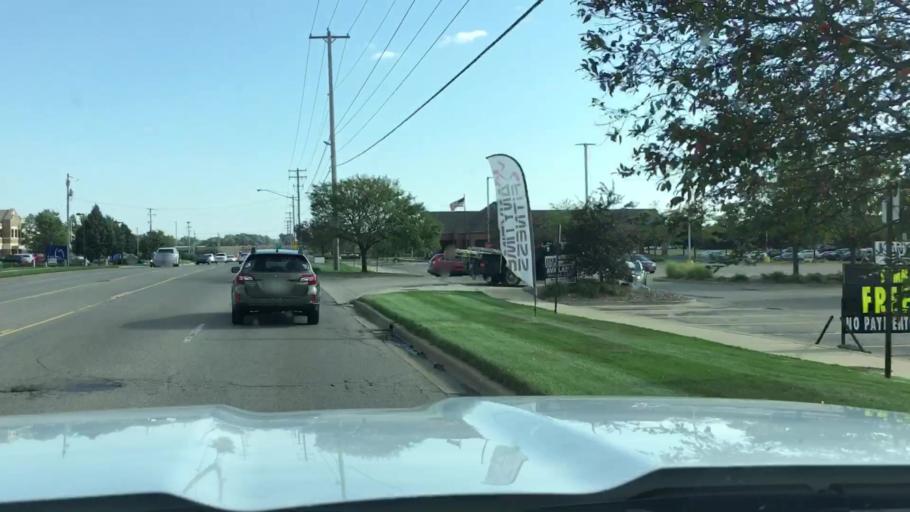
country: US
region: Michigan
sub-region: Kent County
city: Kentwood
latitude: 42.8528
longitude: -85.6250
